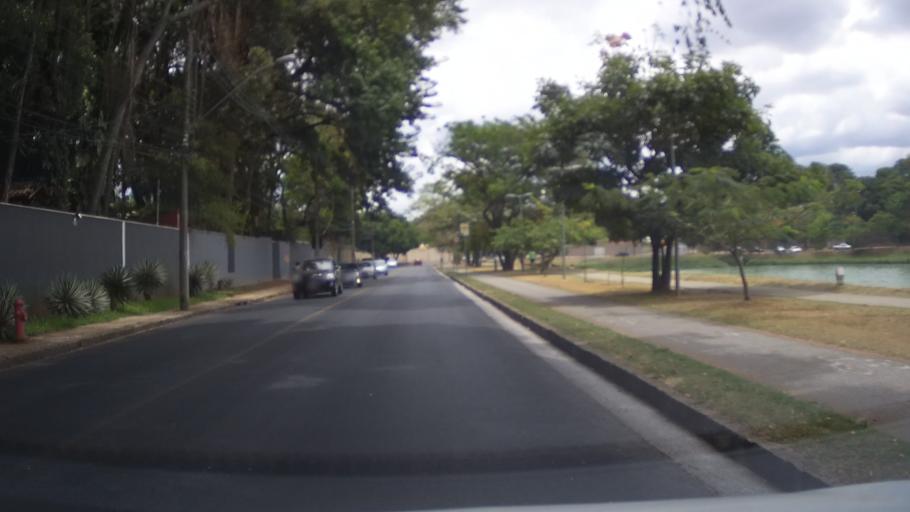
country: BR
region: Minas Gerais
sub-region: Belo Horizonte
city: Belo Horizonte
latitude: -19.8402
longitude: -43.9943
